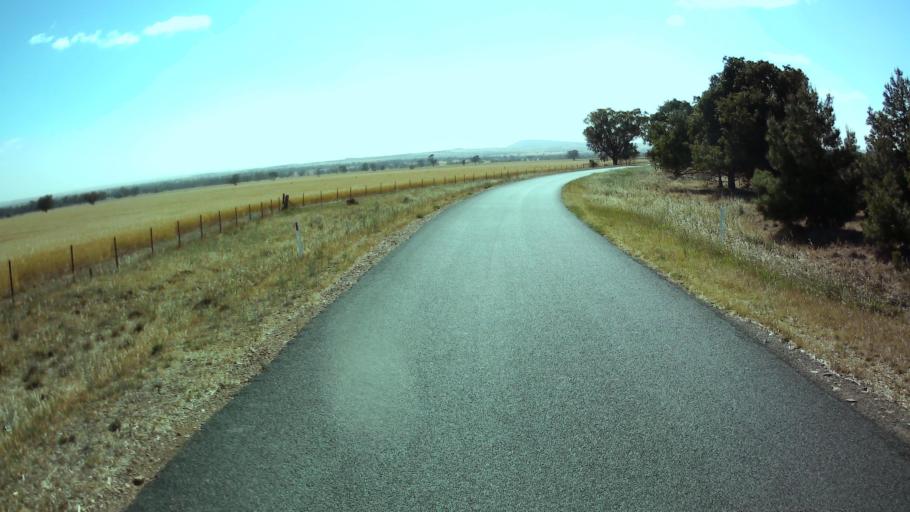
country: AU
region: New South Wales
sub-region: Weddin
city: Grenfell
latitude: -34.0613
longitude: 148.2694
